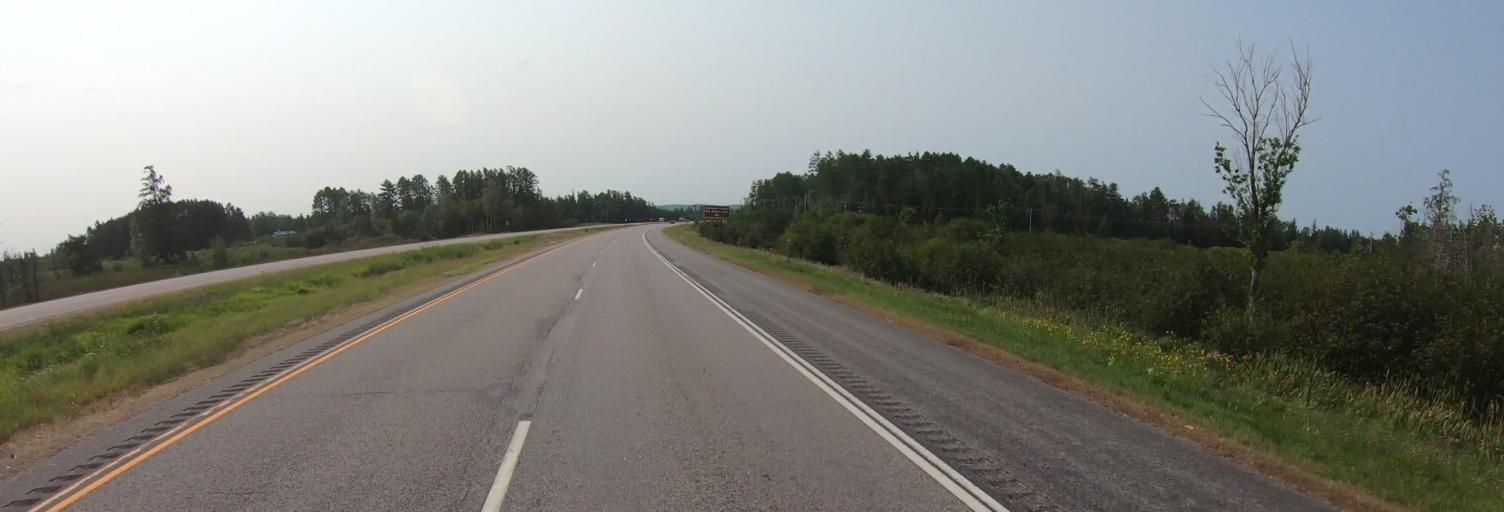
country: US
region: Minnesota
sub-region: Saint Louis County
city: Parkville
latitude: 47.6325
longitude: -92.5563
